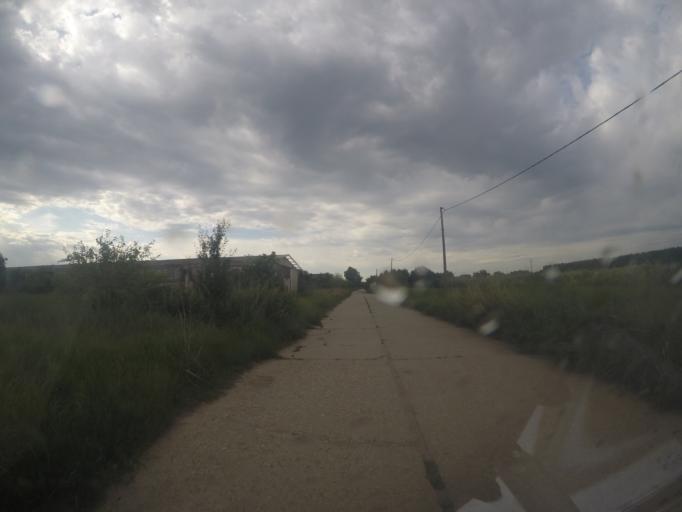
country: RS
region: Central Serbia
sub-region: Belgrade
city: Zemun
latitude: 44.8846
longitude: 20.3831
